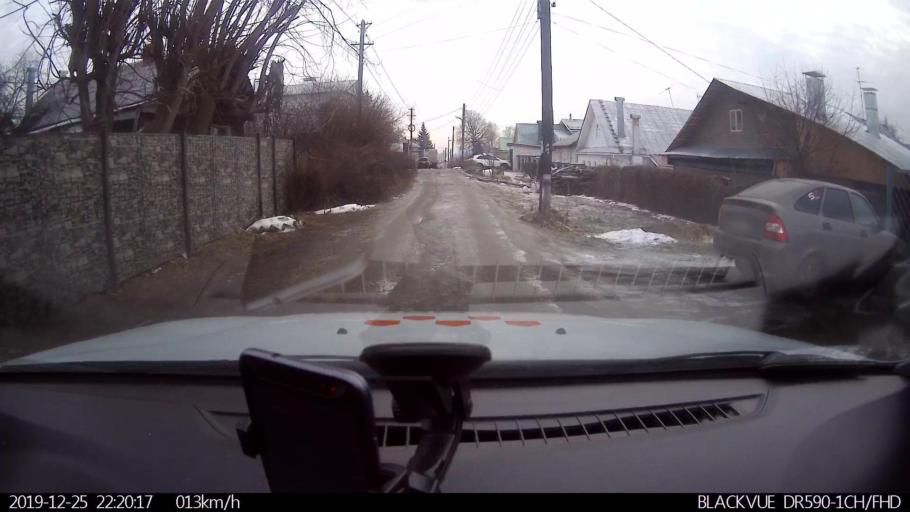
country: RU
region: Nizjnij Novgorod
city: Nizhniy Novgorod
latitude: 56.2553
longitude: 43.9948
